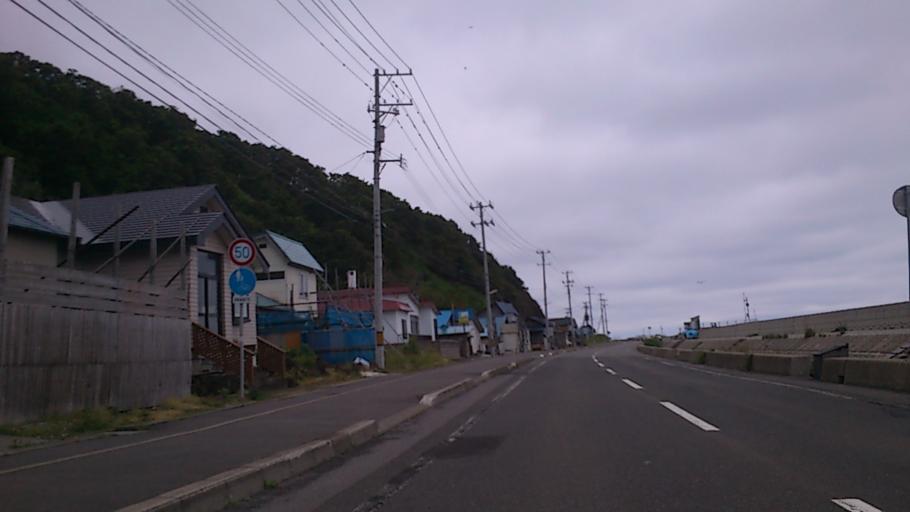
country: JP
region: Hokkaido
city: Iwanai
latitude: 42.7465
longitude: 140.1227
